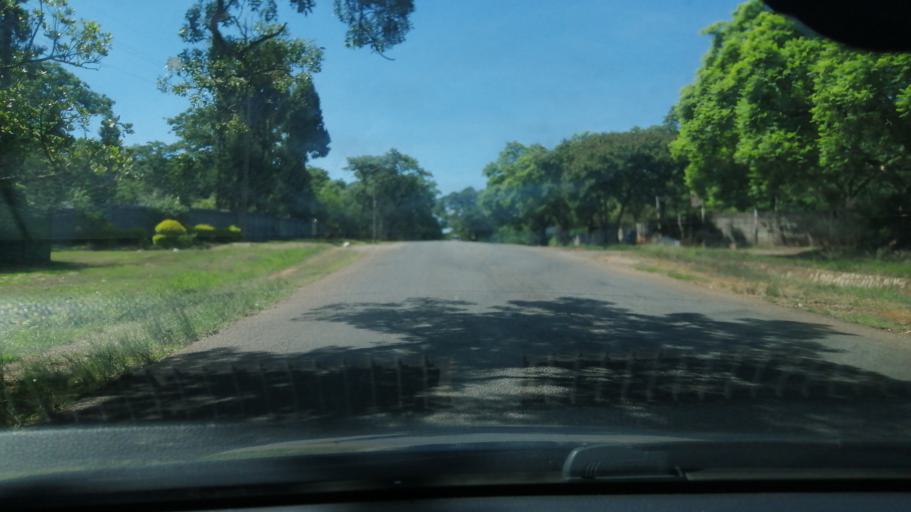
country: ZW
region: Harare
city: Harare
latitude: -17.7996
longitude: 31.1288
